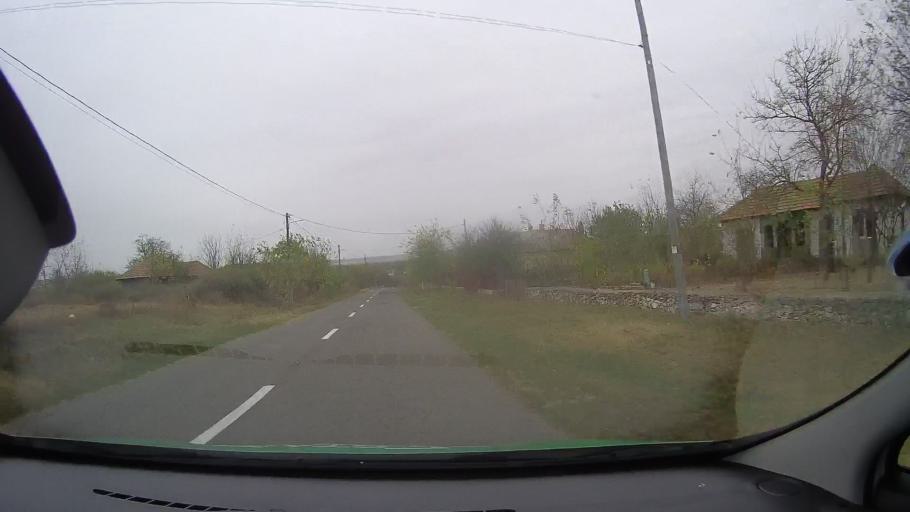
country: RO
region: Constanta
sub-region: Comuna Vulturu
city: Vulturu
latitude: 44.6974
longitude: 28.2414
